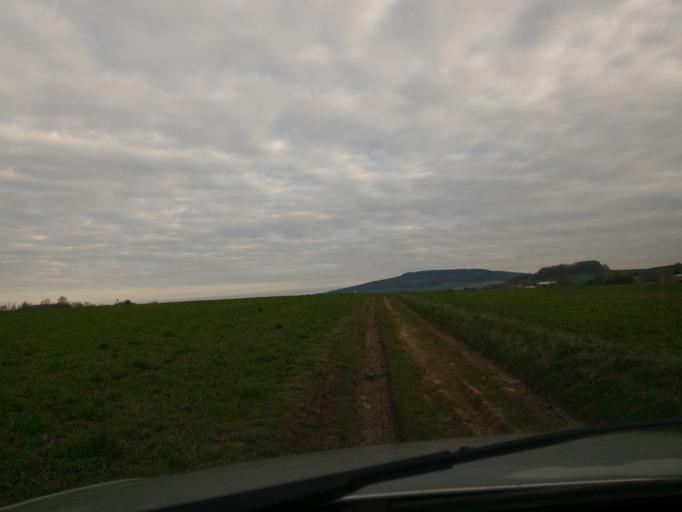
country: DE
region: Saxony
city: Eibau
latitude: 50.9675
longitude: 14.6701
